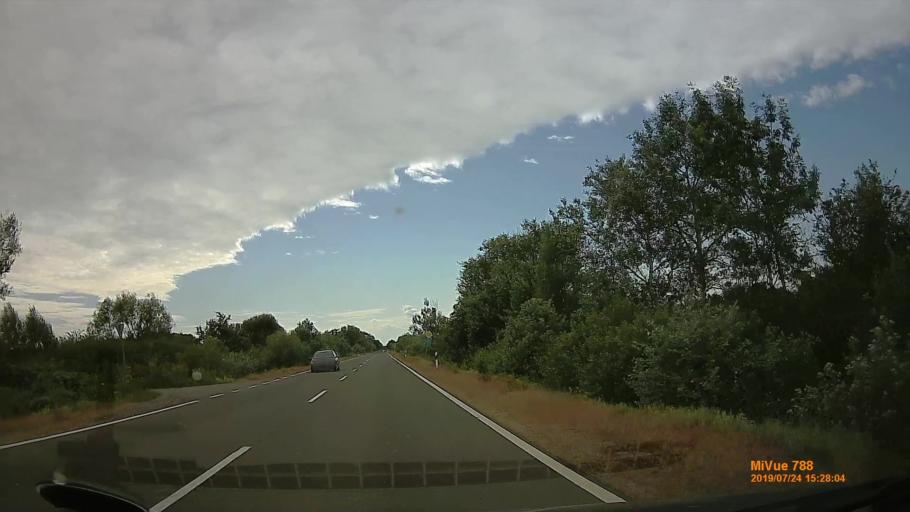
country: HU
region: Szabolcs-Szatmar-Bereg
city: Tarpa
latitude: 48.1608
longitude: 22.4860
